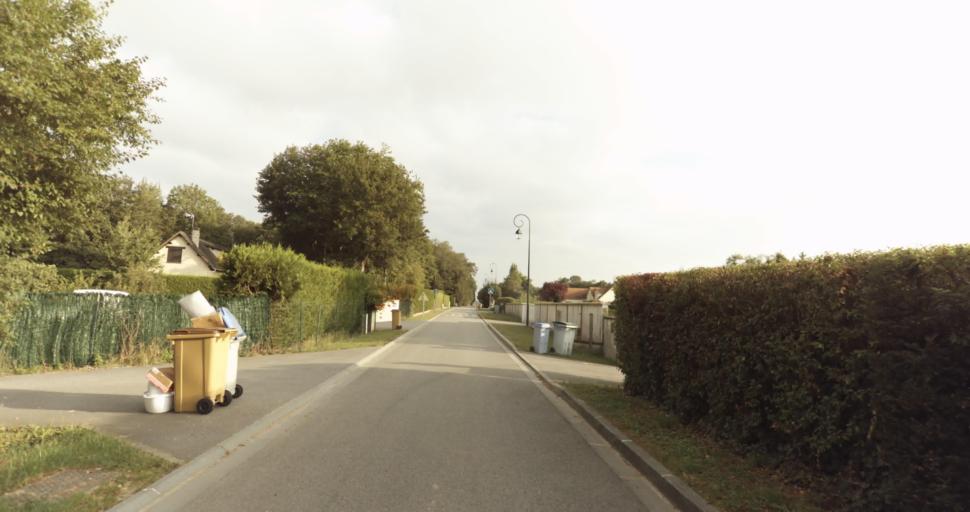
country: FR
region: Centre
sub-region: Departement d'Eure-et-Loir
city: Vert-en-Drouais
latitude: 48.7837
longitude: 1.3162
